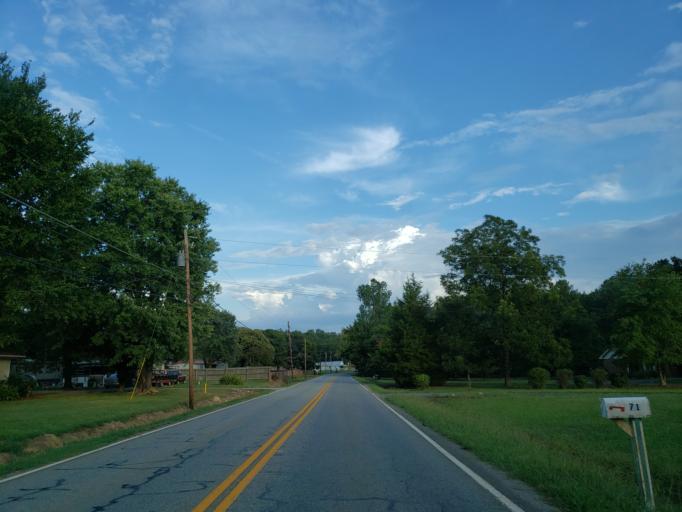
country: US
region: Georgia
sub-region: Bartow County
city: Cartersville
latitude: 34.2301
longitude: -84.8599
